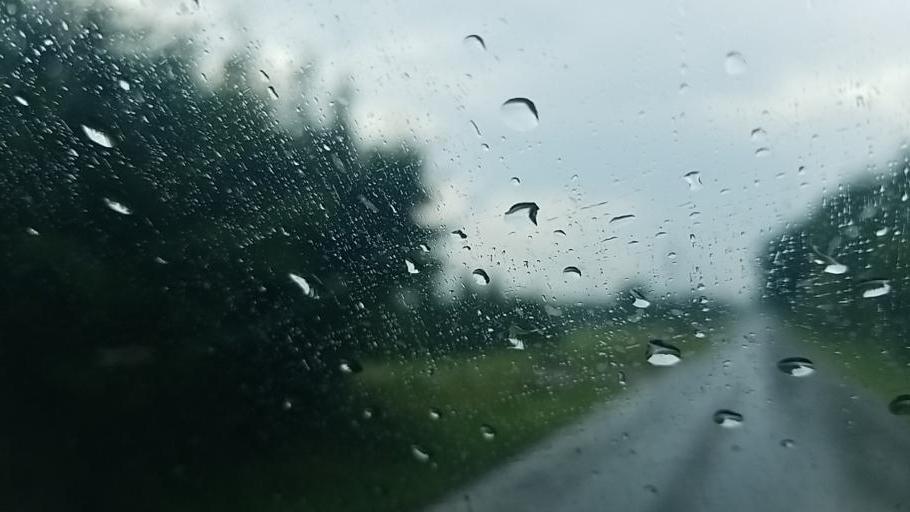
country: US
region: Ohio
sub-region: Lorain County
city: Grafton
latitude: 41.1584
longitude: -82.0348
